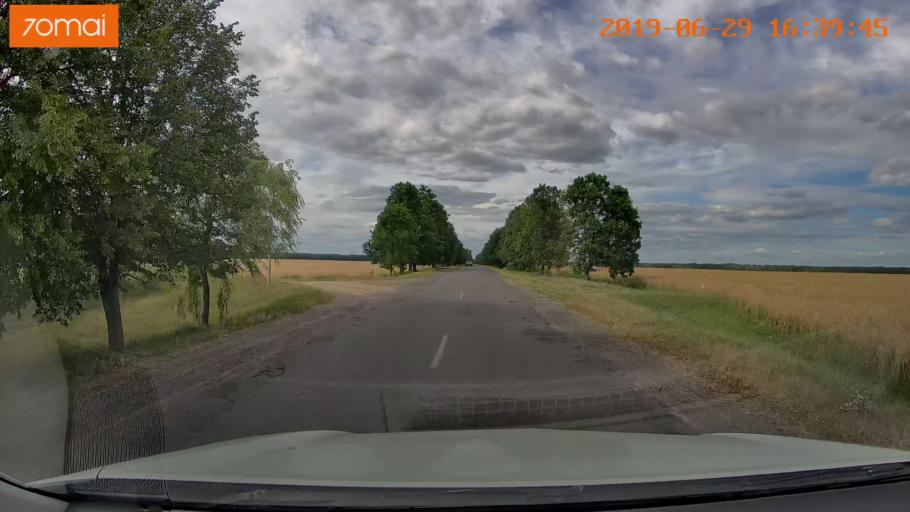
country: BY
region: Brest
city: Luninyets
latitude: 52.2463
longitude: 27.0165
